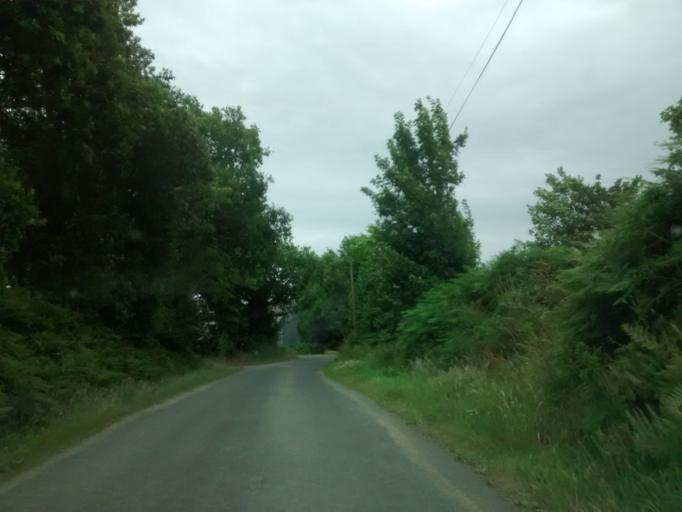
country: FR
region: Brittany
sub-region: Departement des Cotes-d'Armor
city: Trelevern
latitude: 48.7931
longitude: -3.3624
